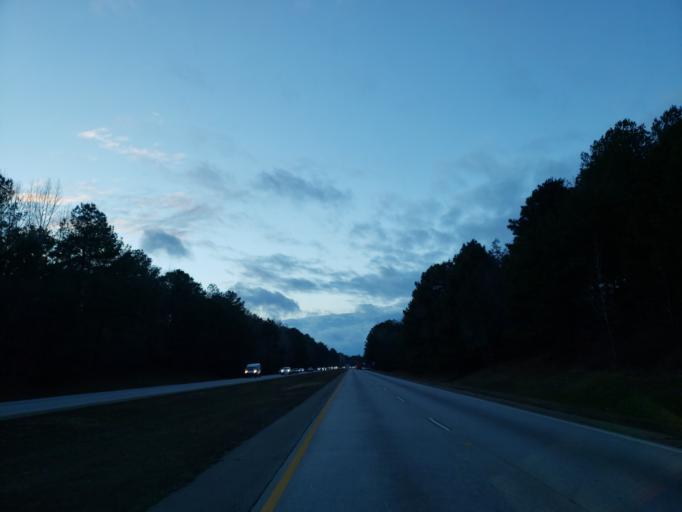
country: US
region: Georgia
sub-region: Fulton County
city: Union City
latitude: 33.6828
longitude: -84.5594
